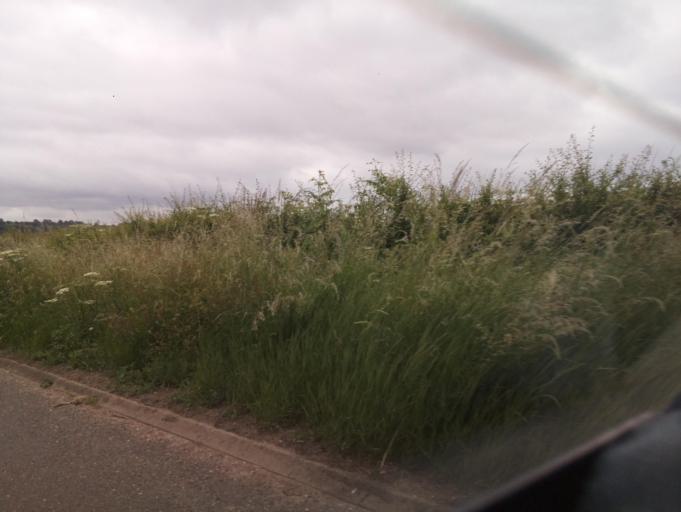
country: GB
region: England
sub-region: District of Rutland
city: Manton
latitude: 52.6266
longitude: -0.7095
